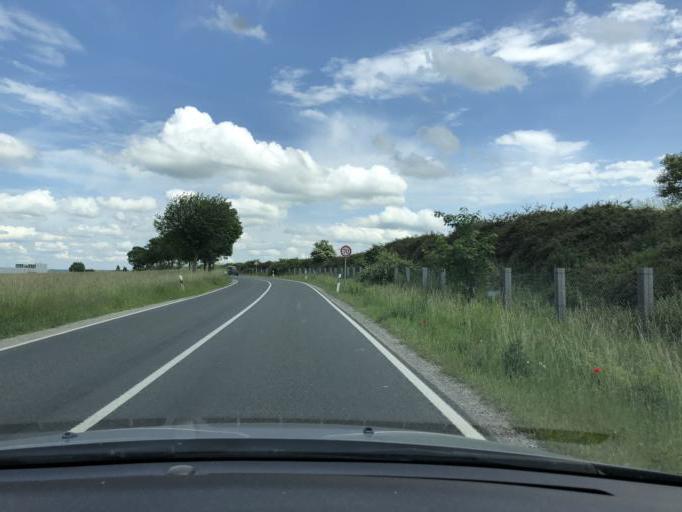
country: DE
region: Thuringia
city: Kefferhausen
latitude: 51.3002
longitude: 10.2814
